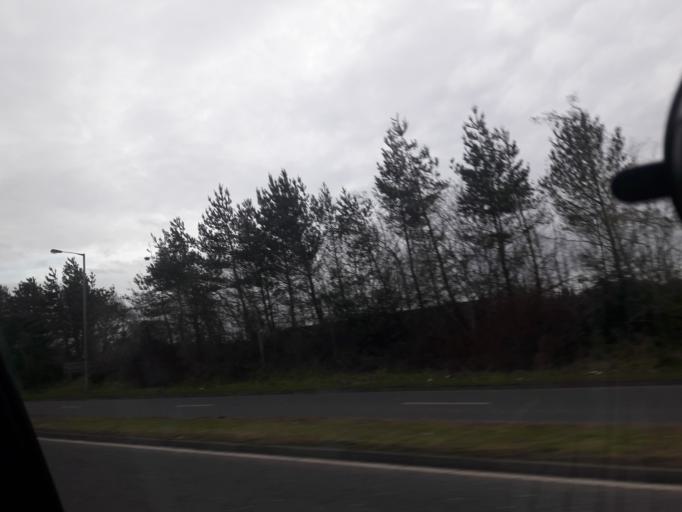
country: GB
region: Northern Ireland
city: Hillsborough
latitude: 54.4902
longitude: -6.0689
